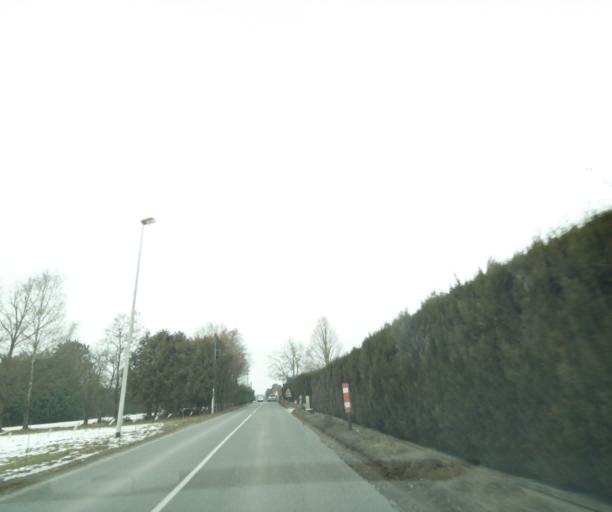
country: FR
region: Rhone-Alpes
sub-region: Departement de la Haute-Savoie
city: Arenthon
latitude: 46.1220
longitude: 6.3128
